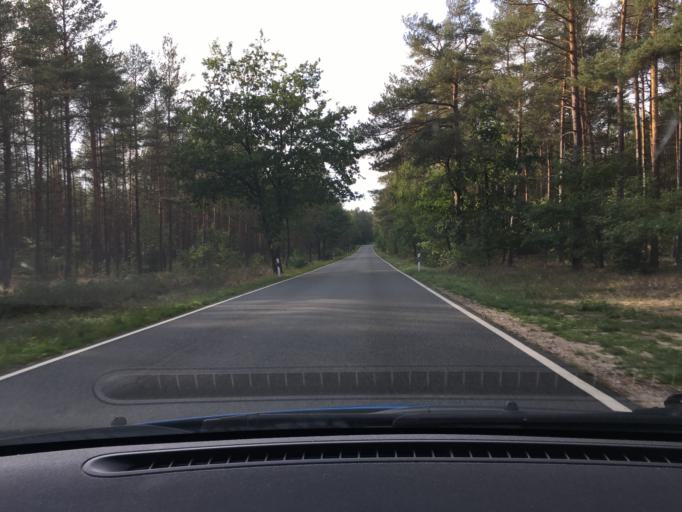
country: DE
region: Lower Saxony
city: Fassberg
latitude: 52.8992
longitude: 10.1113
